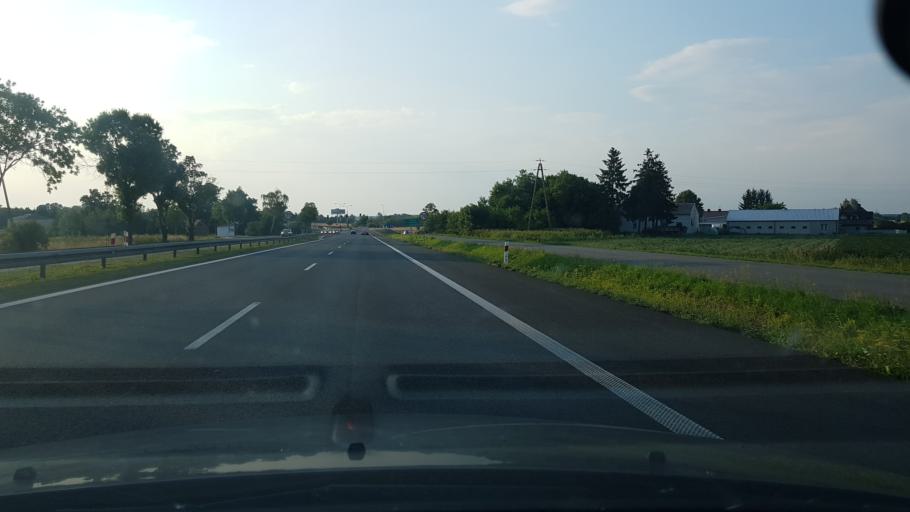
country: PL
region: Masovian Voivodeship
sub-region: Powiat plonski
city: Zaluski
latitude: 52.4741
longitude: 20.5661
